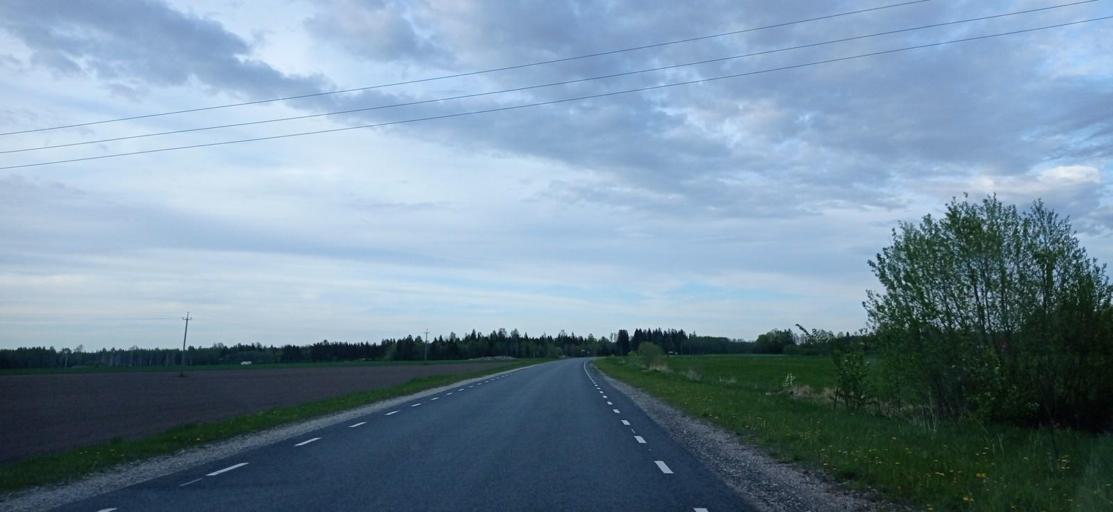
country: EE
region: Paernumaa
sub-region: Tootsi vald
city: Tootsi
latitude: 58.5376
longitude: 24.7279
